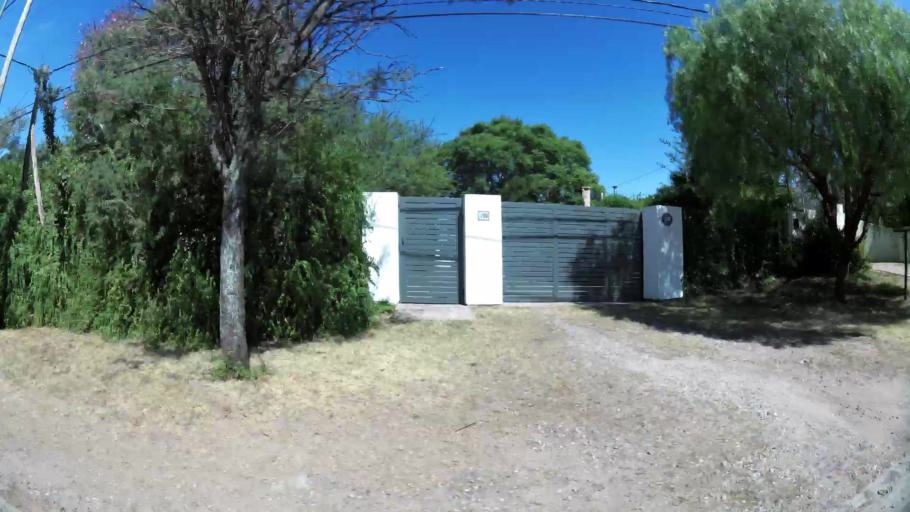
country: AR
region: Cordoba
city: Villa Allende
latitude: -31.2993
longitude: -64.2834
